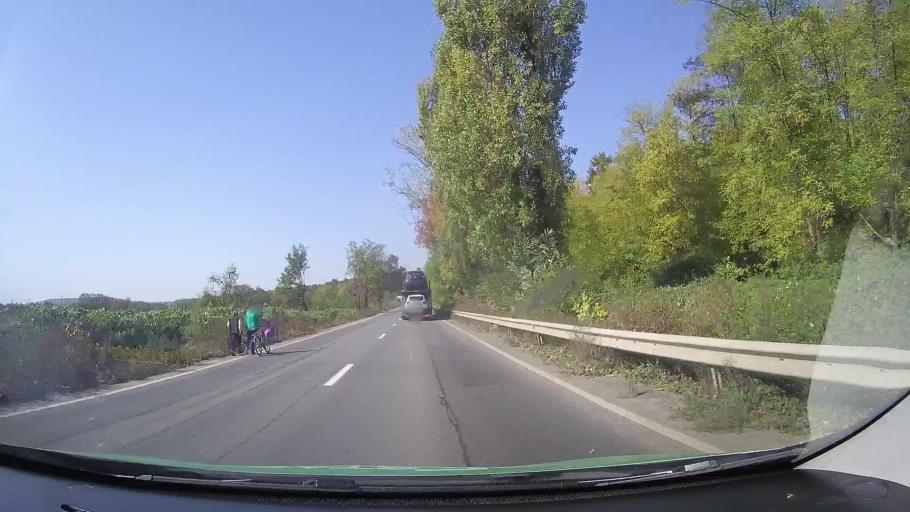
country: RO
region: Arad
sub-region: Comuna Conop
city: Conop
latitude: 46.1089
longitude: 21.8635
